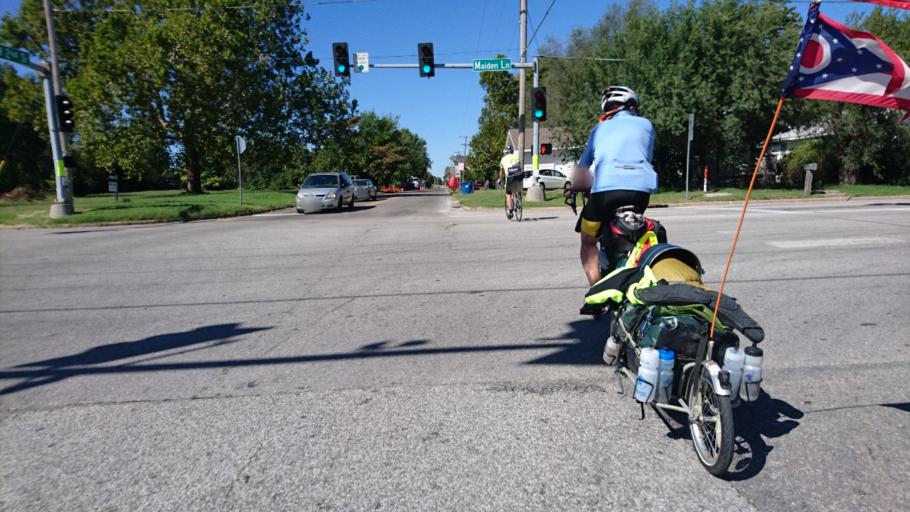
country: US
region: Missouri
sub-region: Jasper County
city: Joplin
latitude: 37.0902
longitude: -94.5307
